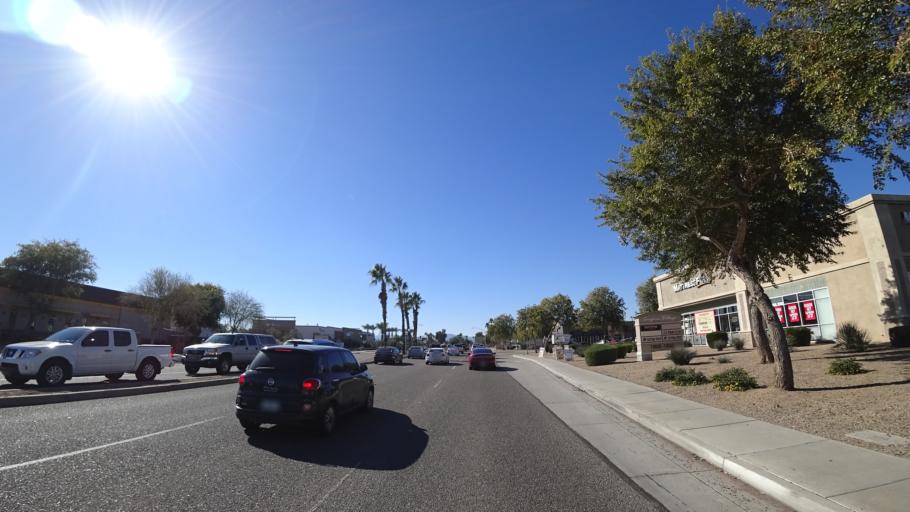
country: US
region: Arizona
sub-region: Maricopa County
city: Surprise
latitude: 33.6387
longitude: -112.3574
